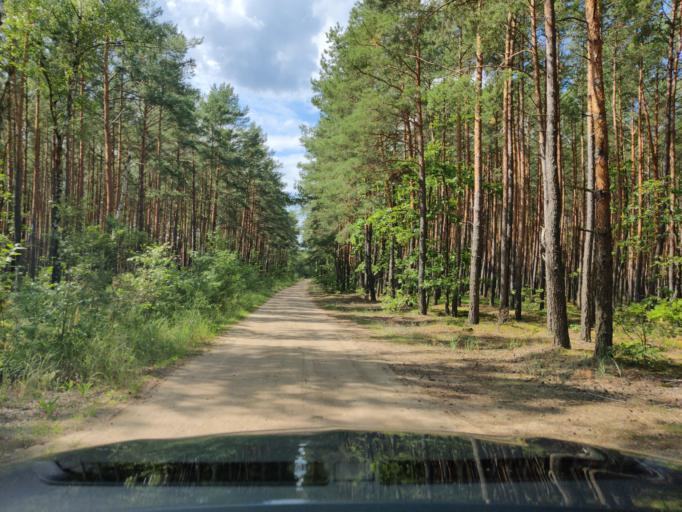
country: PL
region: Masovian Voivodeship
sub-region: Powiat pultuski
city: Pultusk
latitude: 52.7339
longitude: 21.1571
